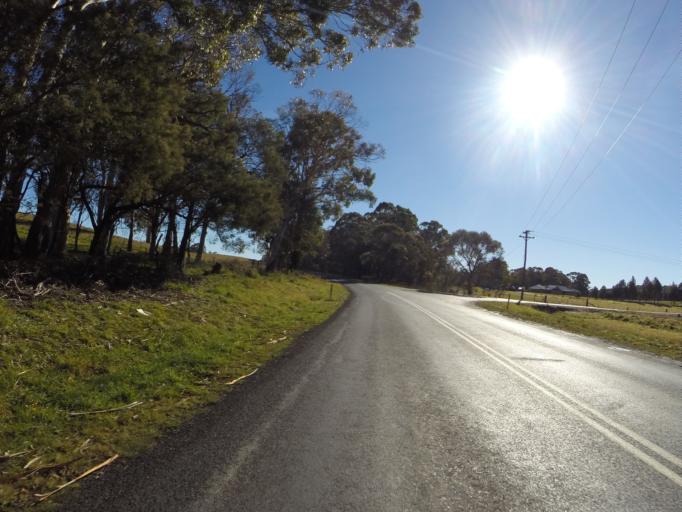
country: AU
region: New South Wales
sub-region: Oberon
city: Oberon
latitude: -33.6770
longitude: 149.8595
